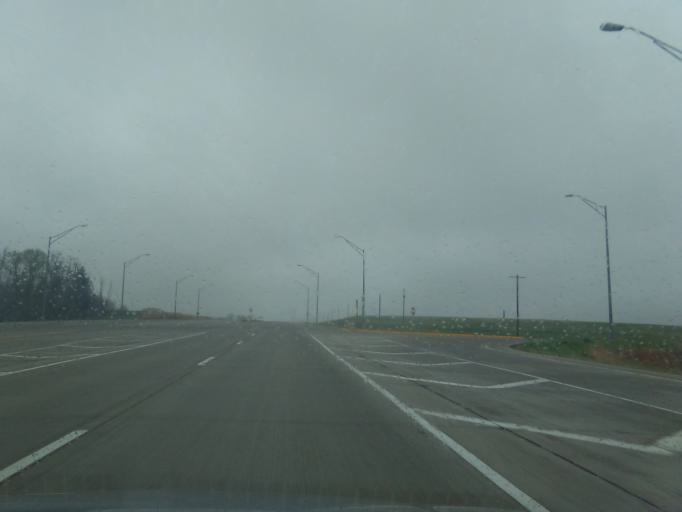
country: US
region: Nebraska
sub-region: Madison County
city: Norfolk
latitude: 42.0669
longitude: -97.3435
